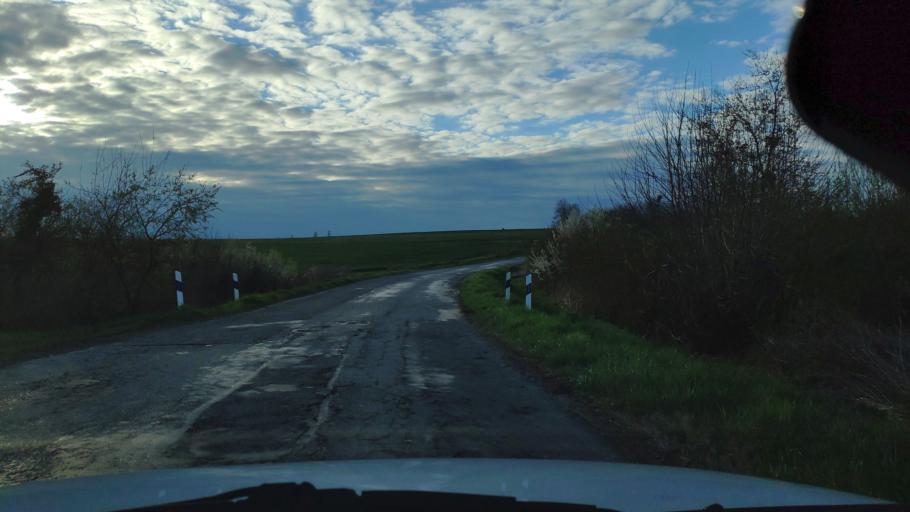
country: HU
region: Zala
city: Nagykanizsa
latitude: 46.4268
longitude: 17.0652
